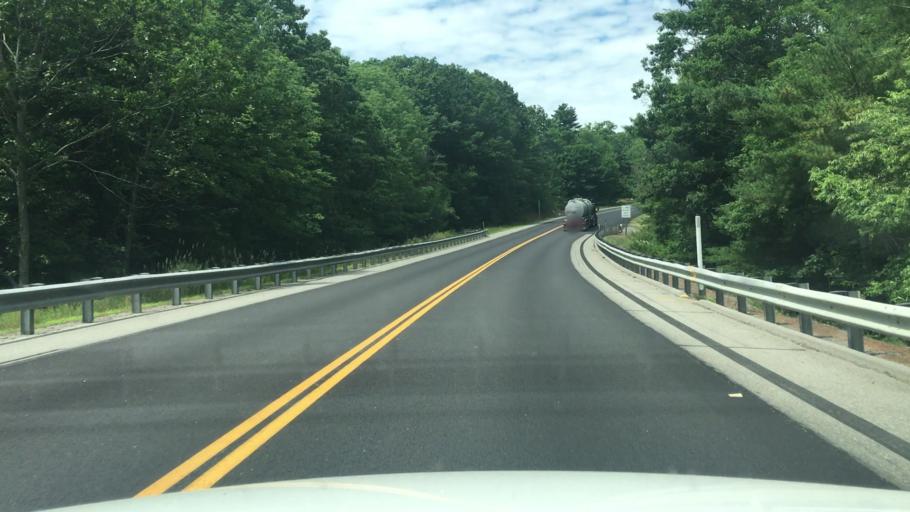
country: US
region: Maine
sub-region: Waldo County
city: Searsmont
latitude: 44.4006
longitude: -69.2910
